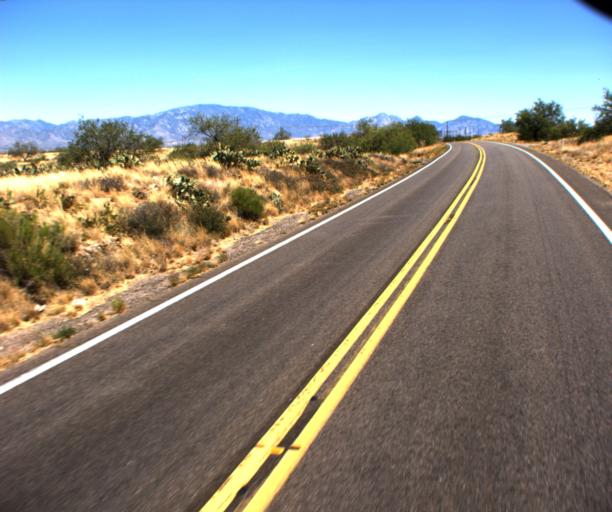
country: US
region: Arizona
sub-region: Pima County
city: Catalina
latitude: 32.6081
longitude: -110.9864
